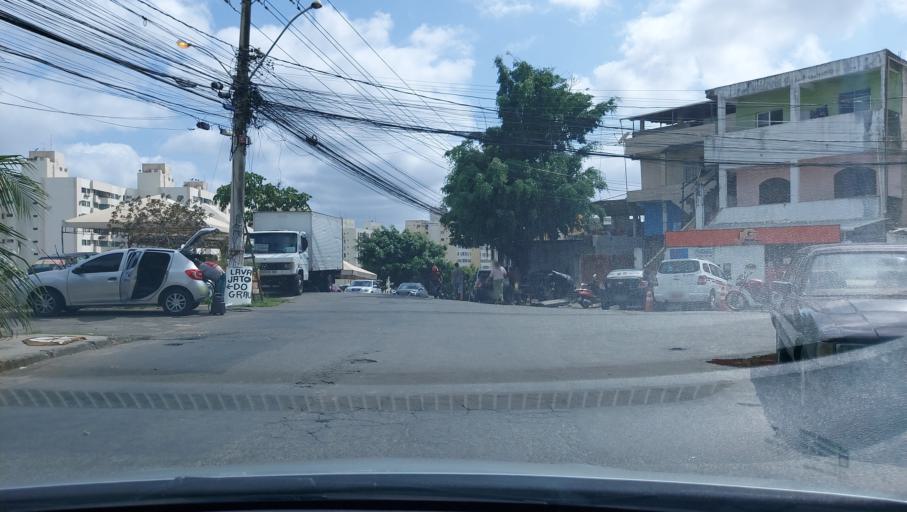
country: BR
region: Bahia
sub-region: Salvador
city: Salvador
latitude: -12.9759
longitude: -38.4367
